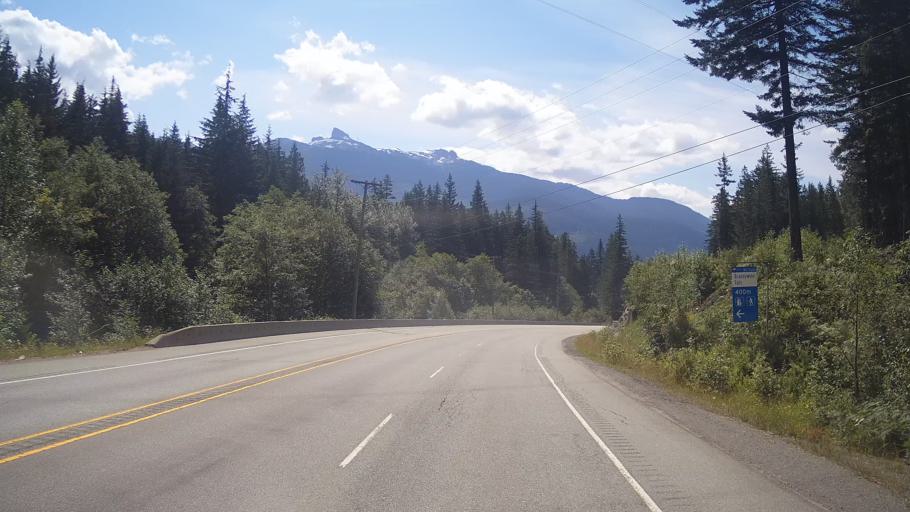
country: CA
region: British Columbia
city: Whistler
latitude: 50.0428
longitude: -123.1242
